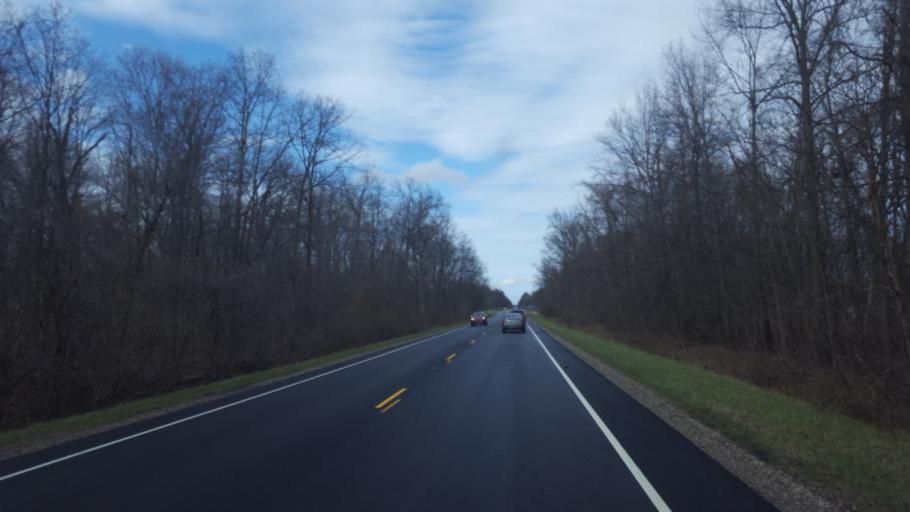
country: US
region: Ohio
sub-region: Franklin County
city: Westerville
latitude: 40.1746
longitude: -82.9141
